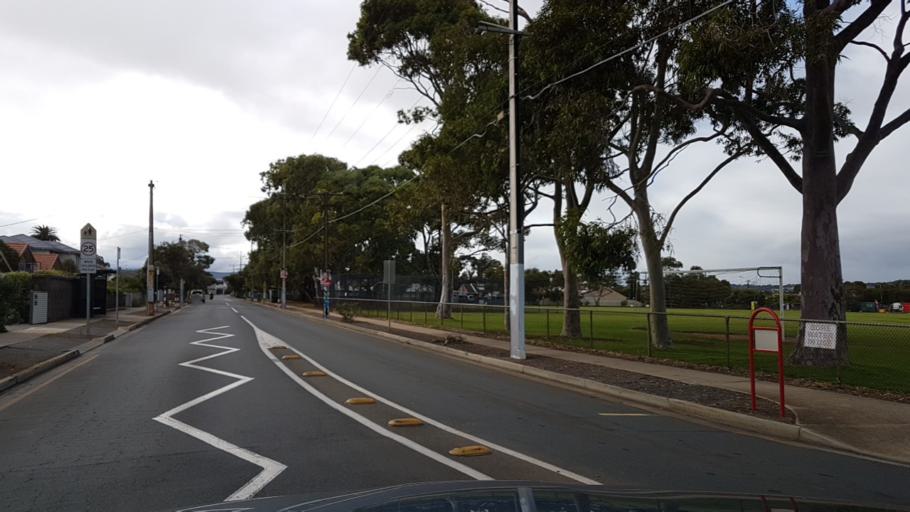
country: AU
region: South Australia
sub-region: Holdfast Bay
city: North Brighton
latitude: -35.0104
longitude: 138.5188
